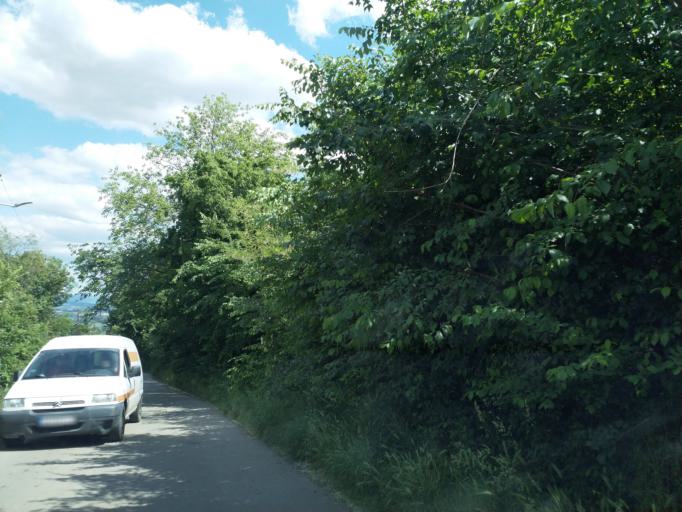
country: RS
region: Central Serbia
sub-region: Pomoravski Okrug
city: Cuprija
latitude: 43.9384
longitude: 21.3154
